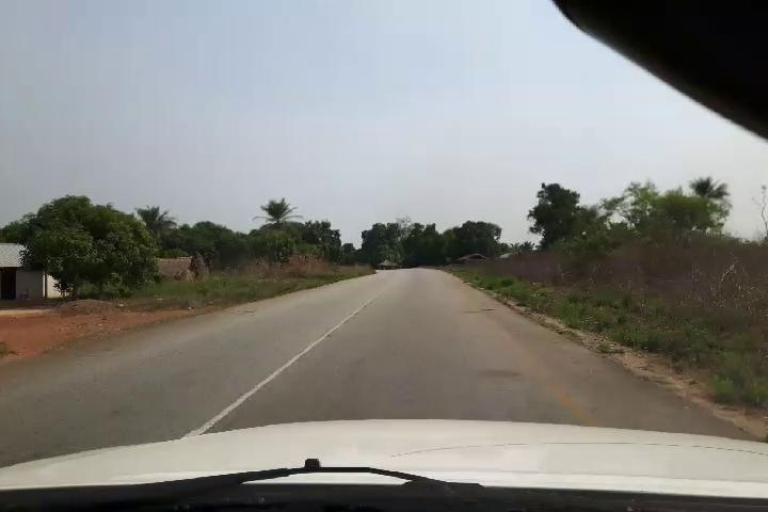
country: SL
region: Southern Province
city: Largo
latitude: 8.3118
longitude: -12.2162
